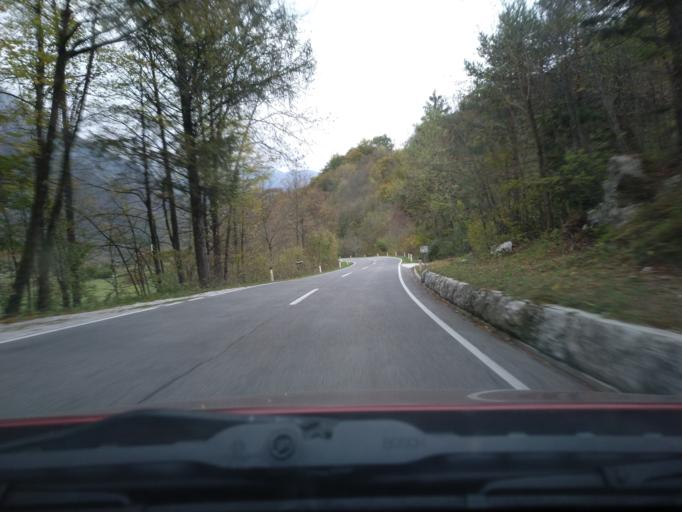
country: SI
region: Kobarid
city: Kobarid
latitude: 46.2816
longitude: 13.5400
